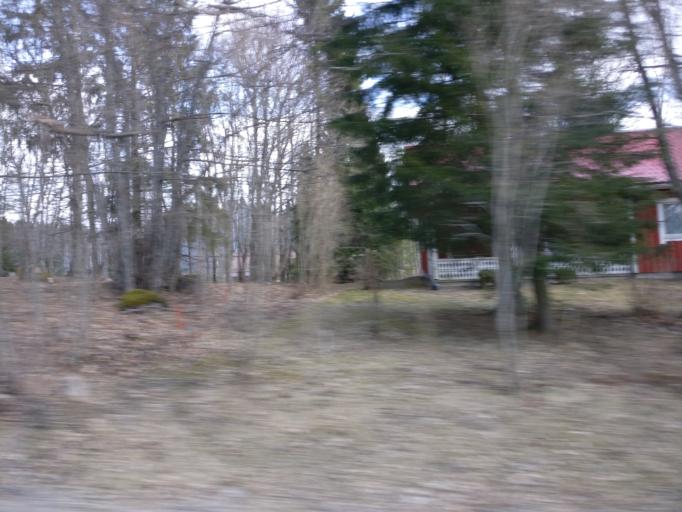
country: FI
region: Uusimaa
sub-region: Helsinki
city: Karjalohja
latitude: 60.2347
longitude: 23.7222
